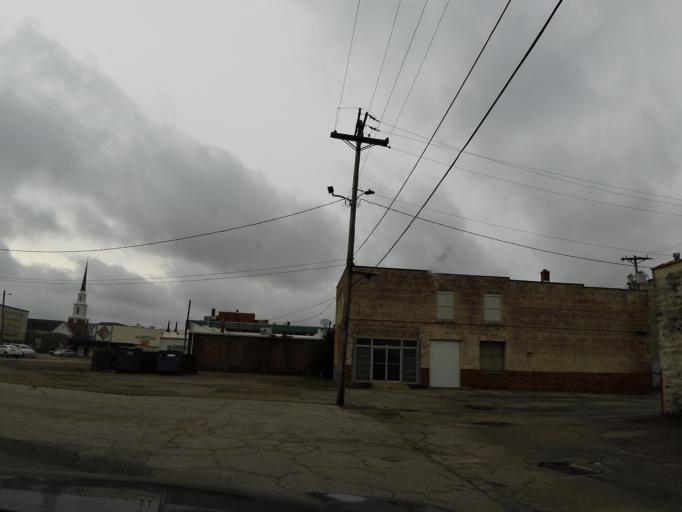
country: US
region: North Carolina
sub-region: Nash County
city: Rocky Mount
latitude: 35.9406
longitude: -77.7971
